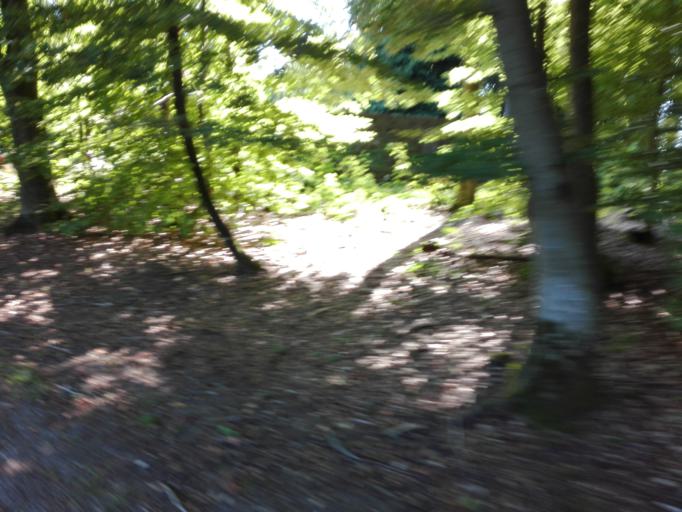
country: DK
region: Central Jutland
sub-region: Odder Kommune
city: Odder
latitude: 55.9661
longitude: 10.1223
